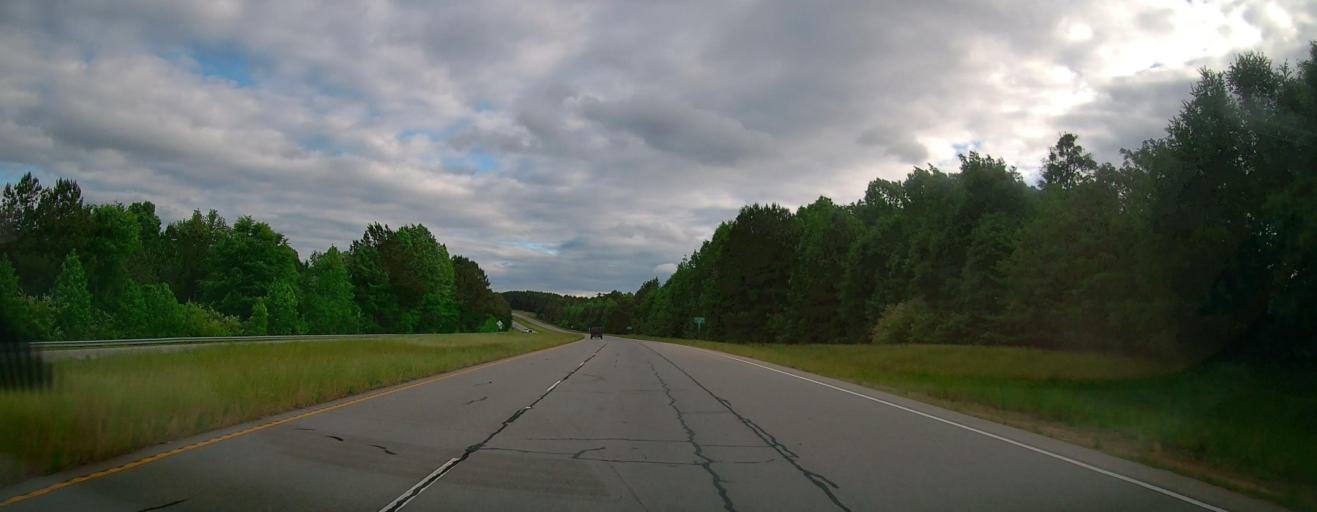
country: US
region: Georgia
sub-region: Oconee County
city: Watkinsville
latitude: 33.8663
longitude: -83.4241
